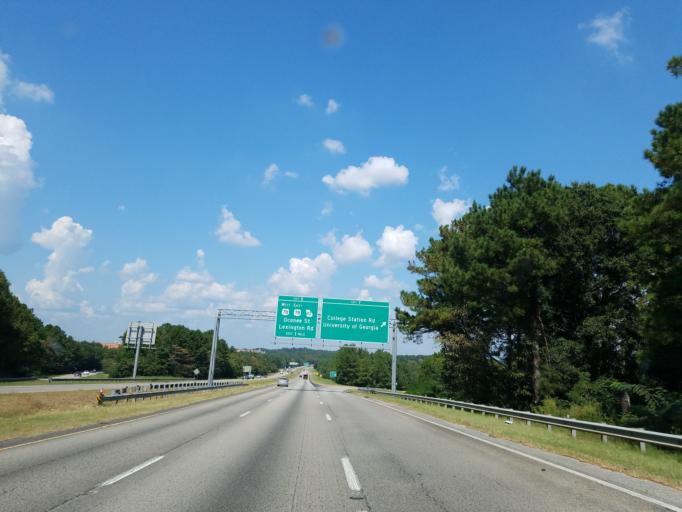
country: US
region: Georgia
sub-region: Clarke County
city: Athens
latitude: 33.9286
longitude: -83.3689
